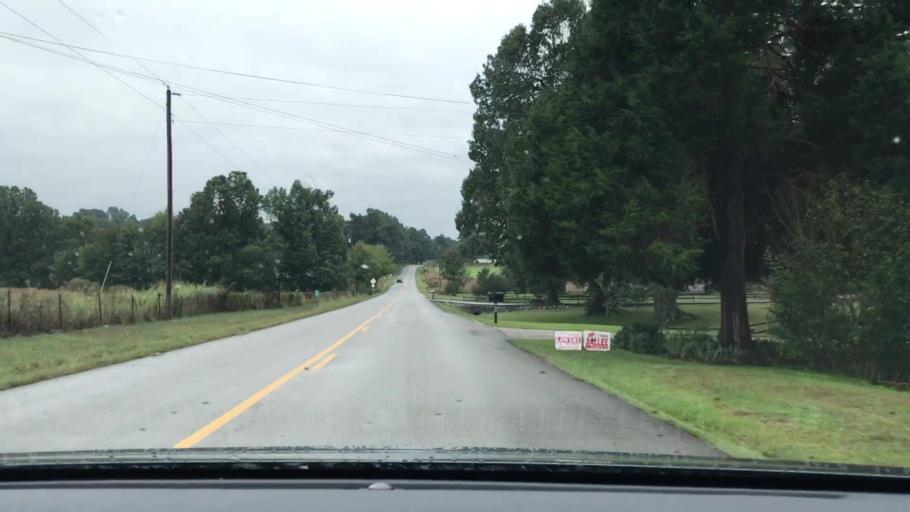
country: US
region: Kentucky
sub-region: McLean County
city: Calhoun
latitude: 37.4841
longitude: -87.2475
